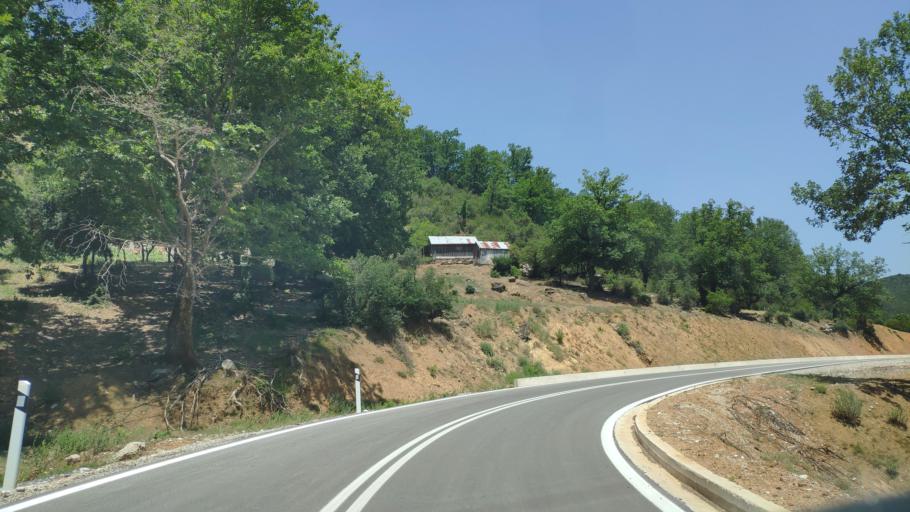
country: GR
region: Epirus
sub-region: Nomos Artas
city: Ano Kalentini
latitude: 39.1812
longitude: 21.3562
